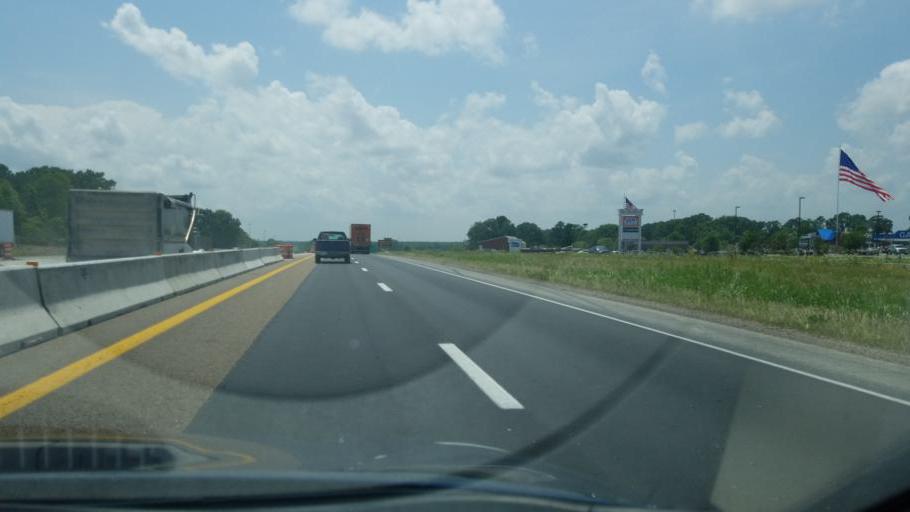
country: US
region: Tennessee
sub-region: Madison County
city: Jackson
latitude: 35.6600
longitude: -88.8660
